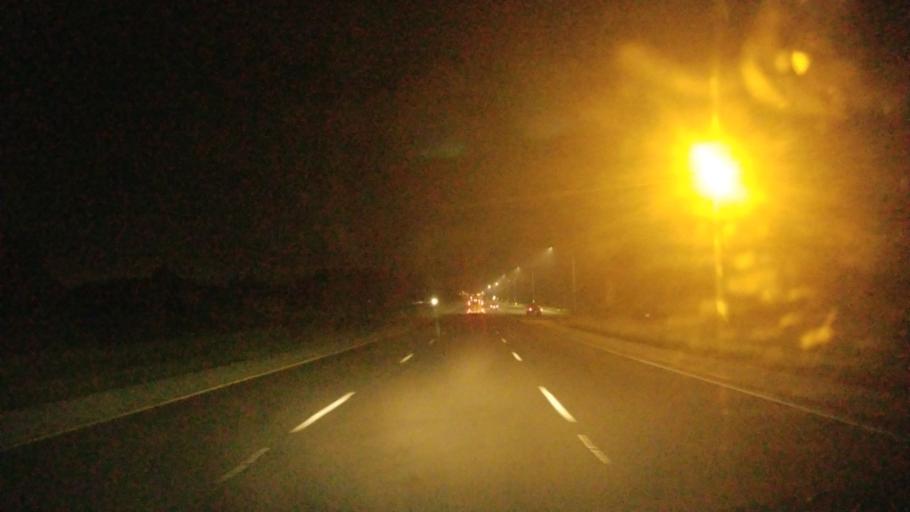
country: US
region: Illinois
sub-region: Madison County
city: Glen Carbon
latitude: 38.7567
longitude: -90.0103
